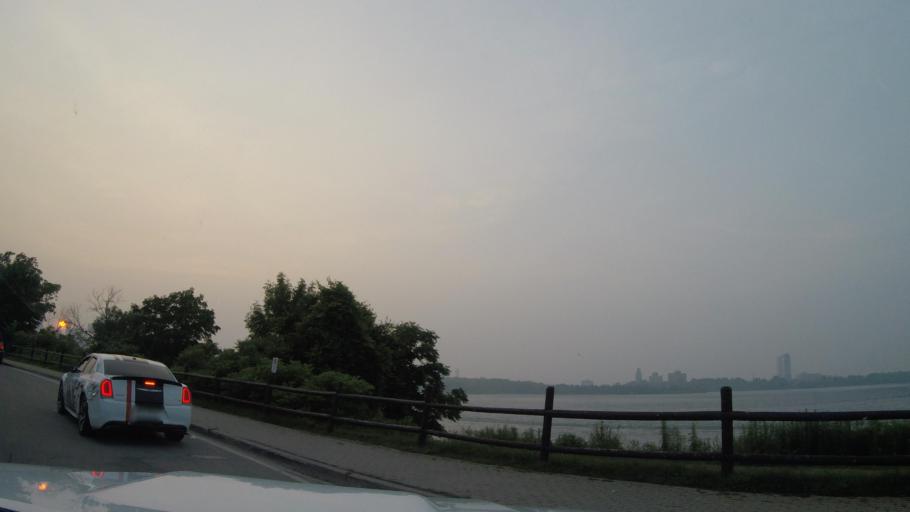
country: US
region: New York
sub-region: Niagara County
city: Niagara Falls
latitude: 43.0696
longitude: -79.0621
